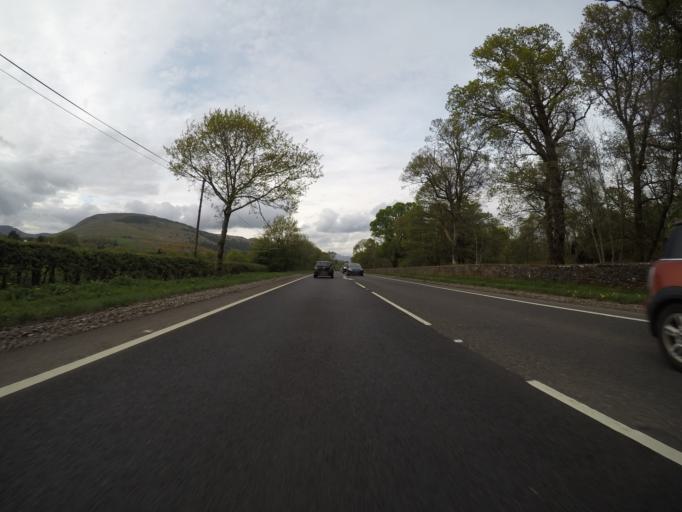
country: GB
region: Scotland
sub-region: West Dunbartonshire
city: Balloch
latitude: 56.0508
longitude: -4.6467
